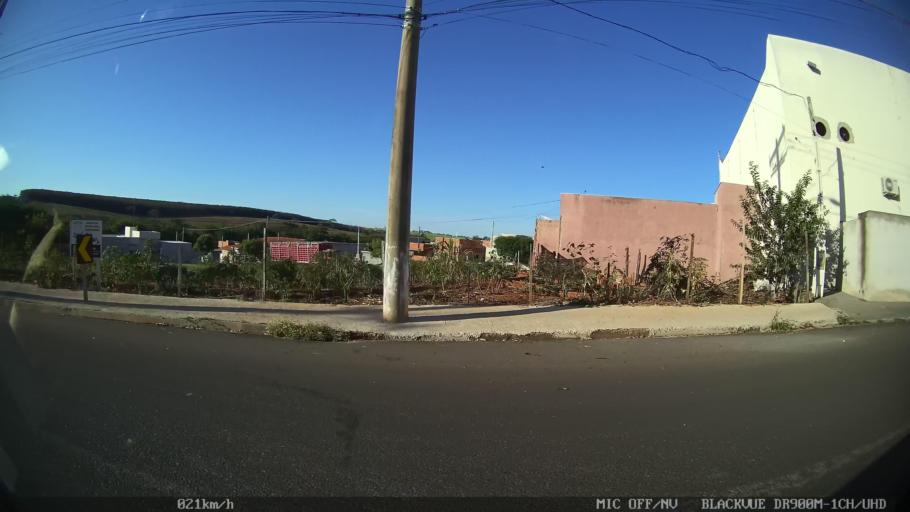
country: BR
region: Sao Paulo
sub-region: Guapiacu
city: Guapiacu
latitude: -20.7894
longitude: -49.2363
